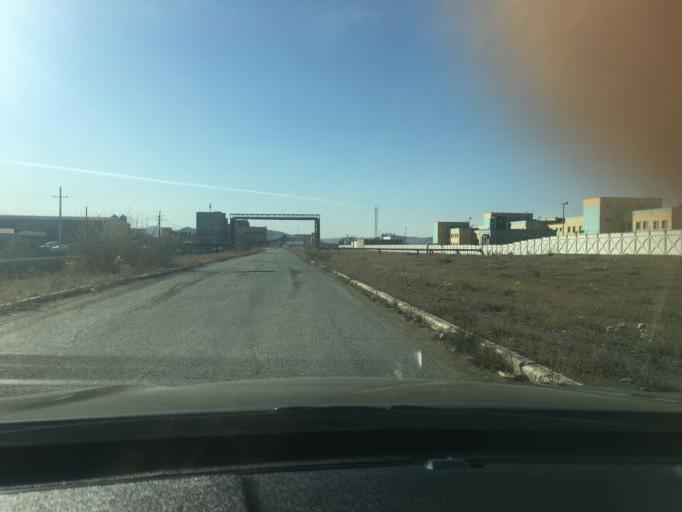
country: MN
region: Ulaanbaatar
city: Ulaanbaatar
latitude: 47.8878
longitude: 106.7772
